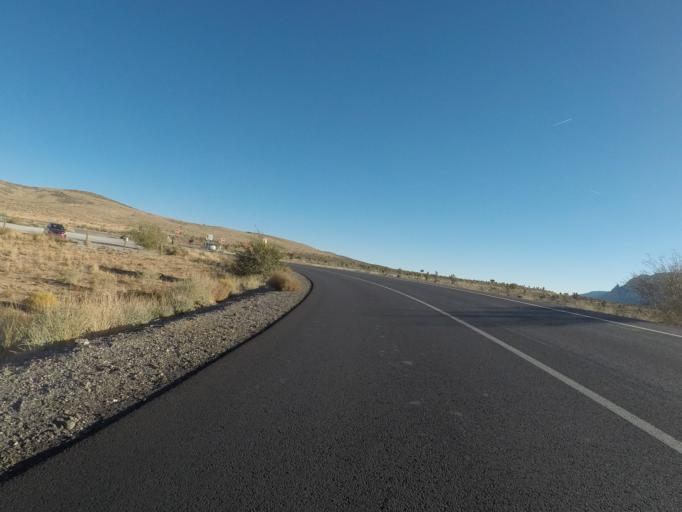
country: US
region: Nevada
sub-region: Clark County
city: Summerlin South
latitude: 36.1117
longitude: -115.4502
